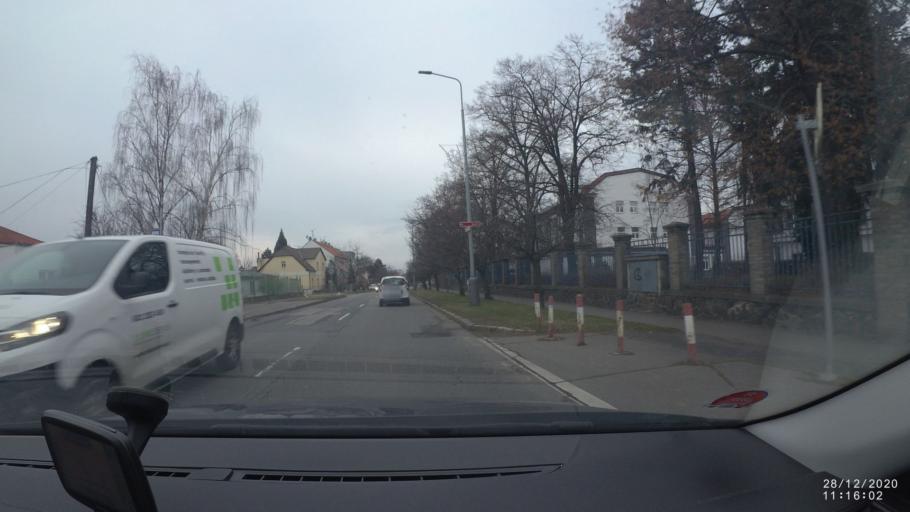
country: CZ
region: Praha
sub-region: Praha 18
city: Letnany
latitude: 50.1330
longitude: 14.5137
